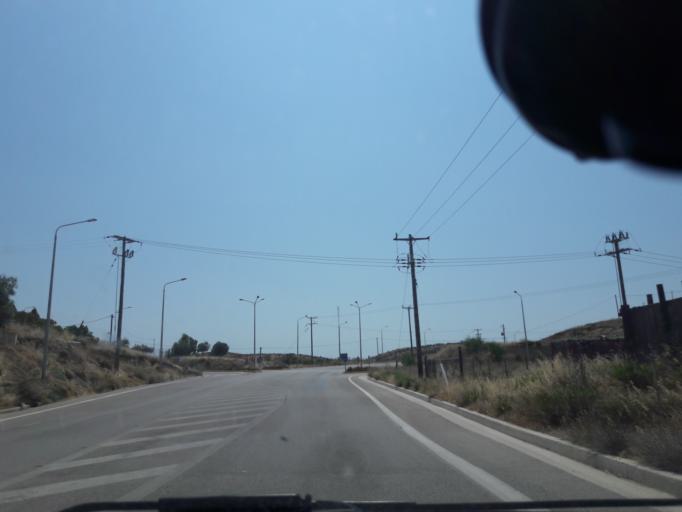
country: GR
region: North Aegean
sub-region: Nomos Lesvou
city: Myrina
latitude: 39.8671
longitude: 25.0737
